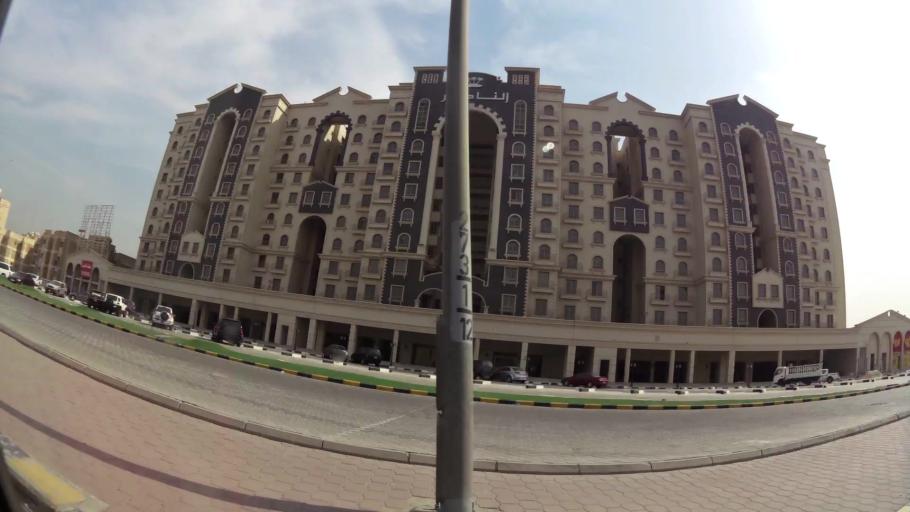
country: KW
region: Al Farwaniyah
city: Al Farwaniyah
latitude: 29.2764
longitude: 47.9693
